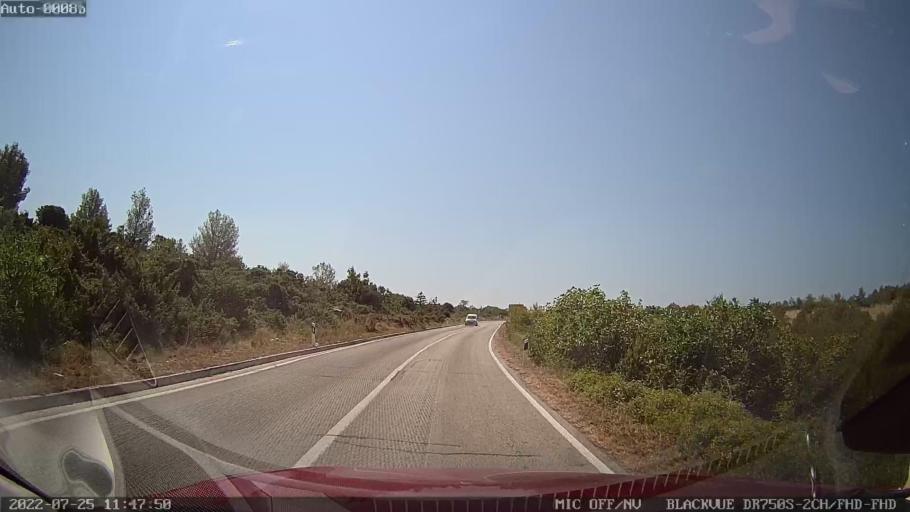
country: HR
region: Zadarska
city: Razanac
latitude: 44.2348
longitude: 15.3026
